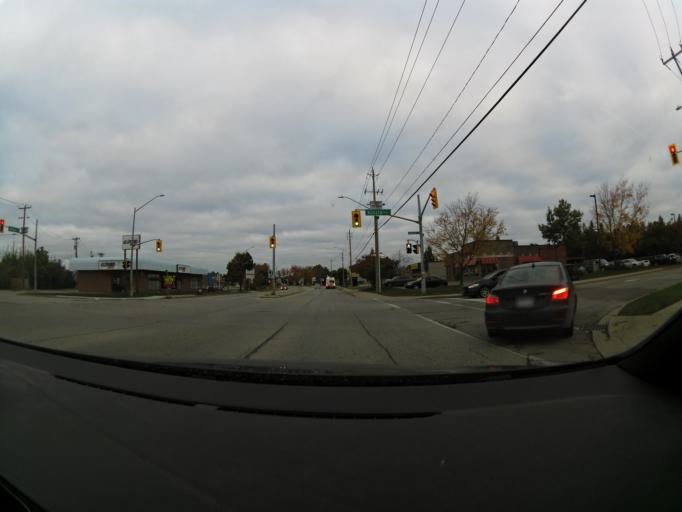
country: CA
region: Ontario
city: Kitchener
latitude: 43.4317
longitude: -80.4384
